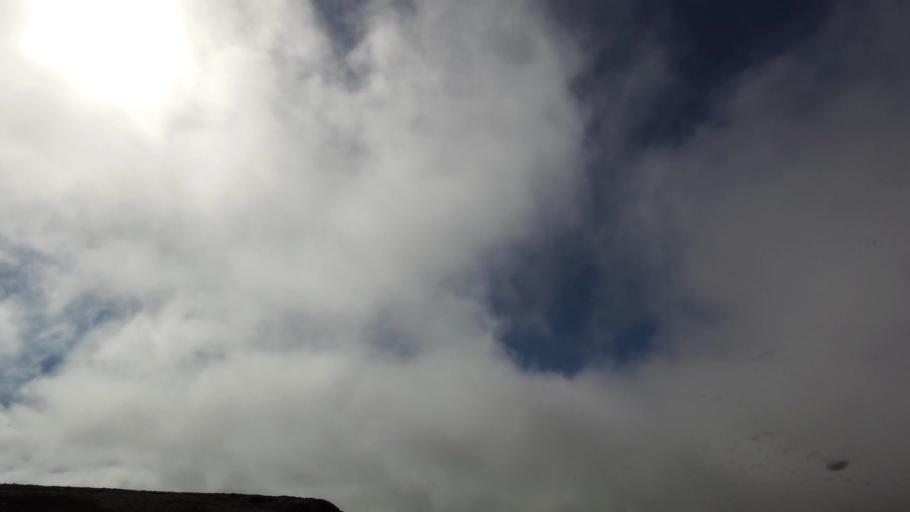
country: IS
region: West
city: Olafsvik
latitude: 65.5581
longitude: -24.2434
